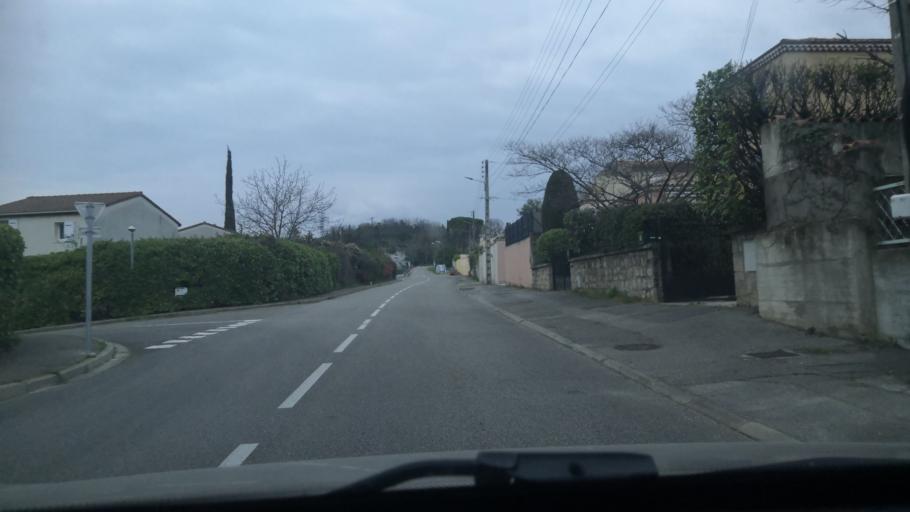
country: FR
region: Rhone-Alpes
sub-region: Departement de la Drome
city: Montelimar
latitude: 44.5772
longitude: 4.7562
